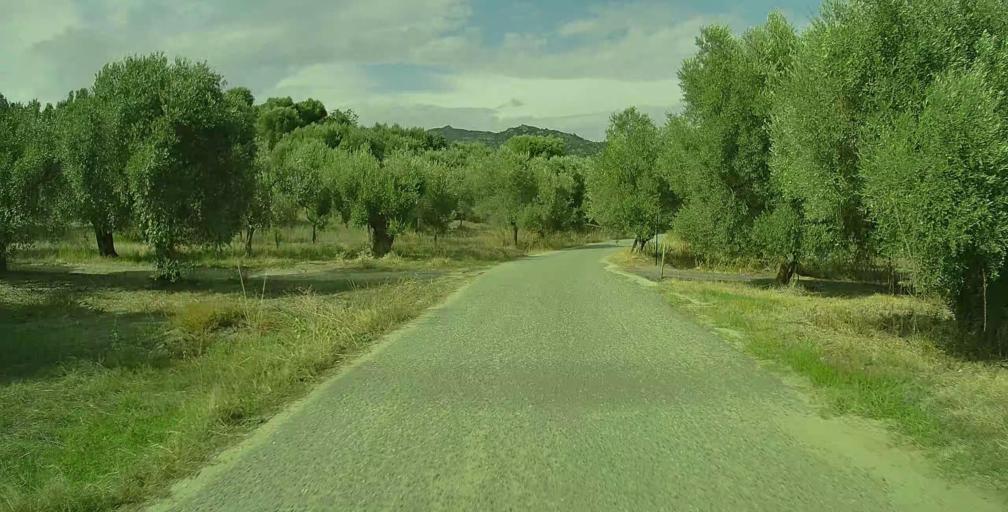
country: GR
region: Central Macedonia
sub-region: Nomos Chalkidikis
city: Sykia
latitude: 40.0347
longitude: 23.9436
